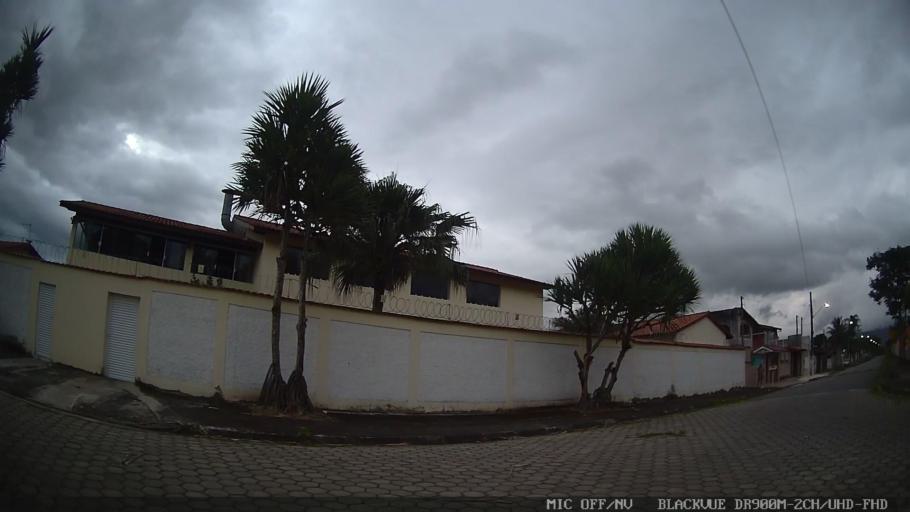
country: BR
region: Sao Paulo
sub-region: Sao Sebastiao
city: Sao Sebastiao
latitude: -23.6960
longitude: -45.4347
